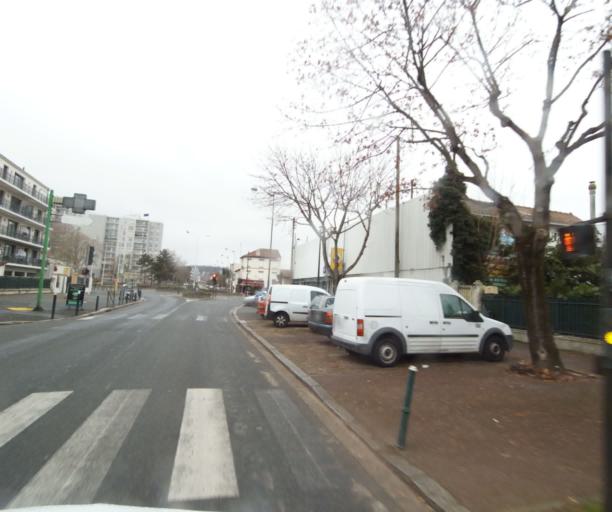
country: FR
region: Ile-de-France
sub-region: Departement des Hauts-de-Seine
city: Rueil-Malmaison
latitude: 48.8881
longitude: 2.1847
